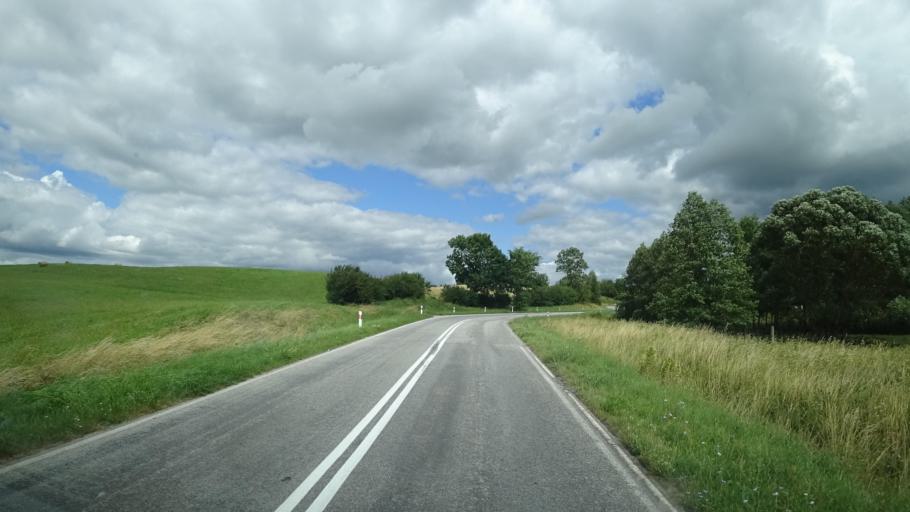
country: PL
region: Warmian-Masurian Voivodeship
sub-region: Powiat goldapski
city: Goldap
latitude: 54.2130
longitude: 22.2164
